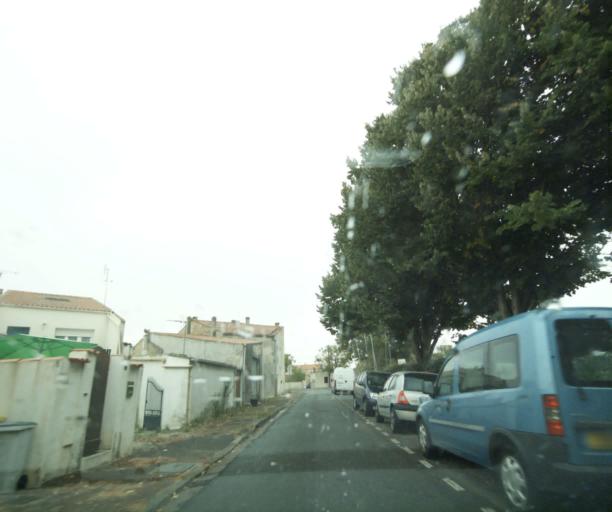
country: FR
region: Poitou-Charentes
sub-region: Departement de la Charente-Maritime
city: Breuil-Magne
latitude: 45.9519
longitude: -0.9421
